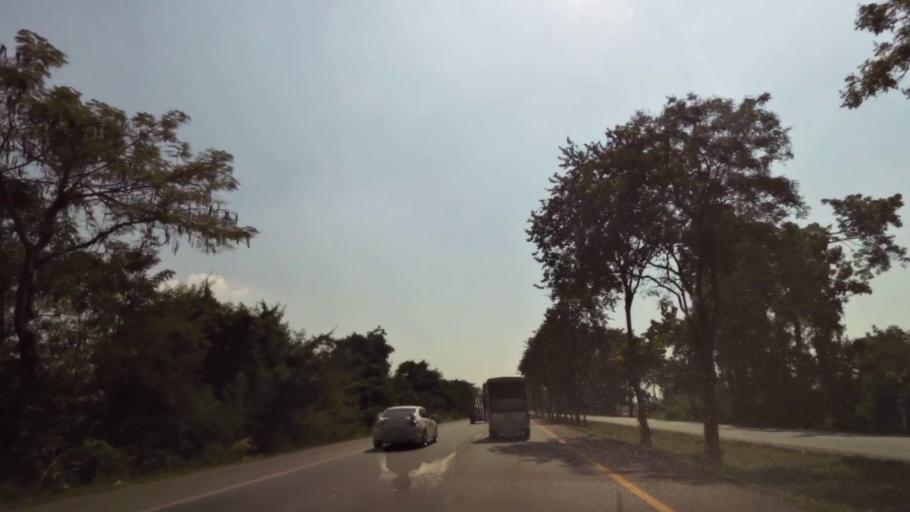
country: TH
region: Phichit
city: Bueng Na Rang
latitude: 16.1124
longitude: 100.1258
